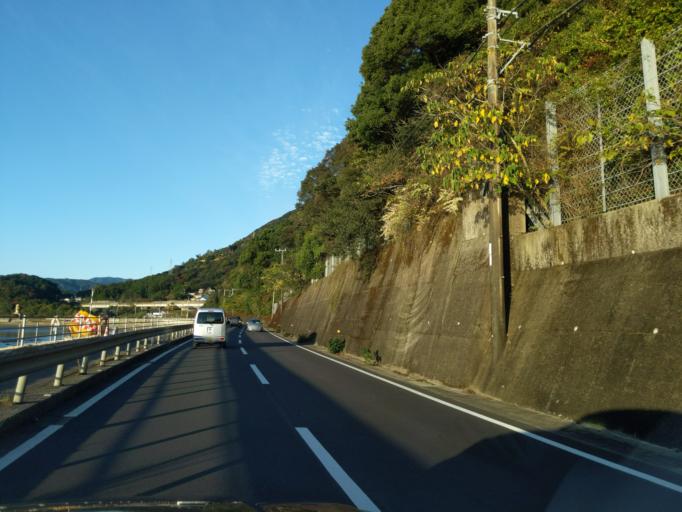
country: JP
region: Kochi
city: Muroto-misakicho
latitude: 33.5827
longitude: 134.3206
